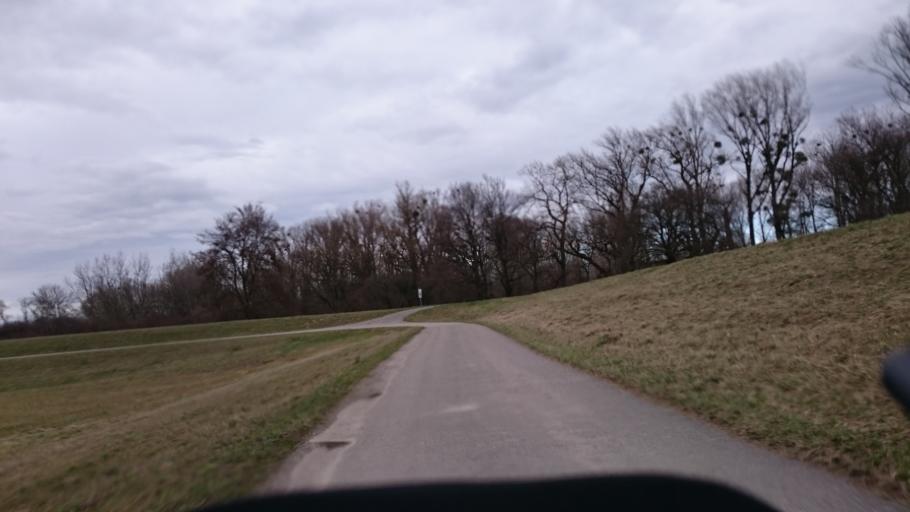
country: DE
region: Rheinland-Pfalz
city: Worth am Rhein
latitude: 49.0181
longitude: 8.2752
